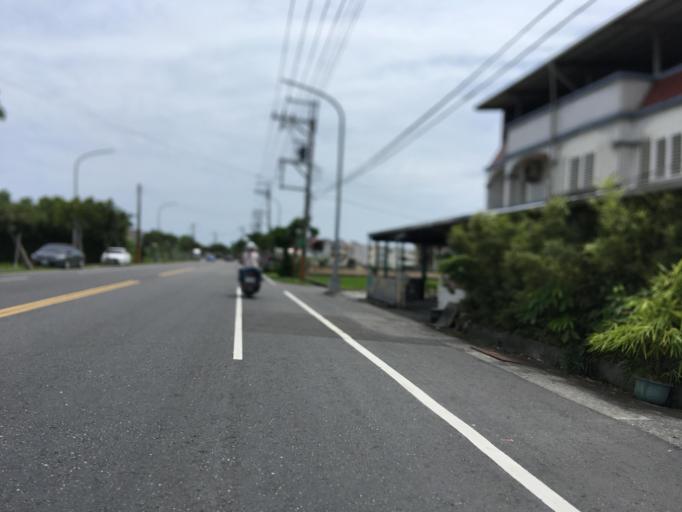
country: TW
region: Taiwan
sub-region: Yilan
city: Yilan
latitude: 24.6888
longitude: 121.8044
